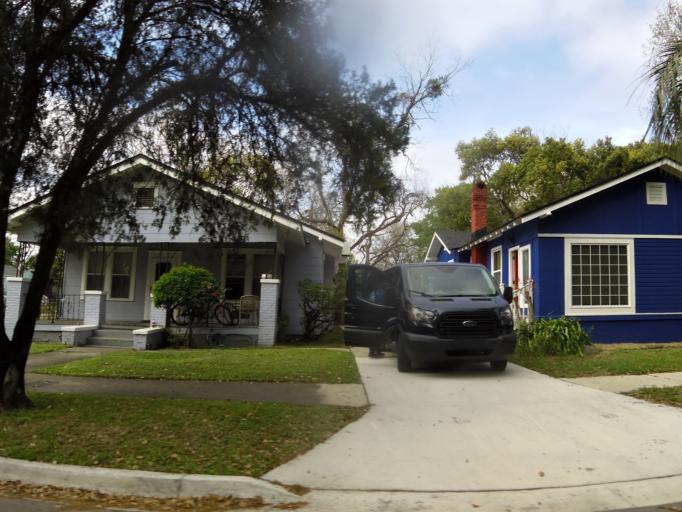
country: US
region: Florida
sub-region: Duval County
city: Jacksonville
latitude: 30.3176
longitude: -81.6953
